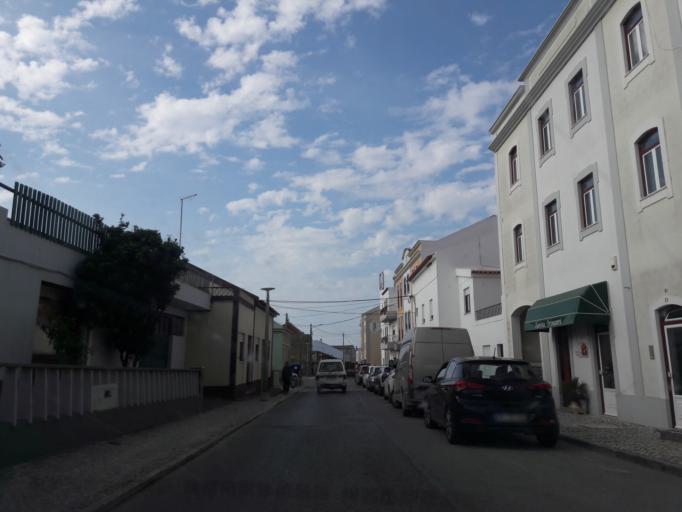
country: PT
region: Leiria
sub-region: Peniche
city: Atouguia da Baleia
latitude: 39.3387
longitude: -9.3275
